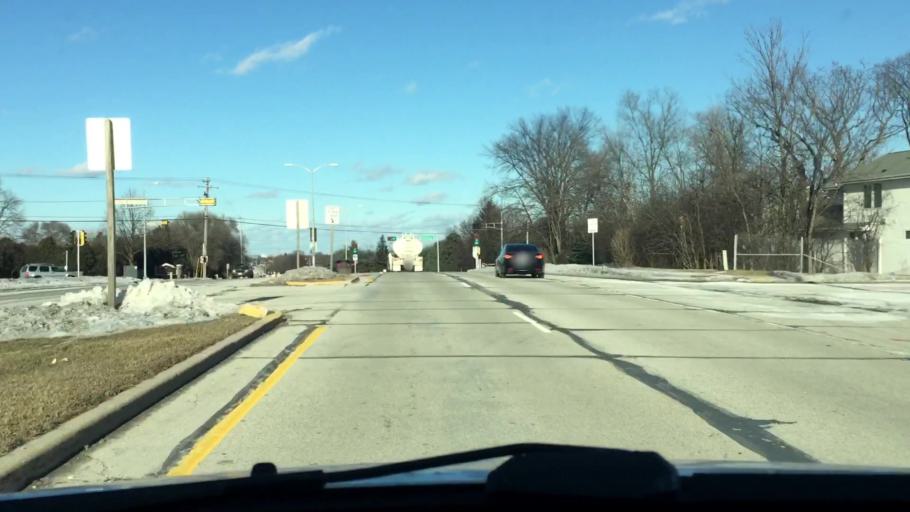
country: US
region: Wisconsin
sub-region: Milwaukee County
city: Greendale
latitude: 42.9660
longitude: -87.9641
